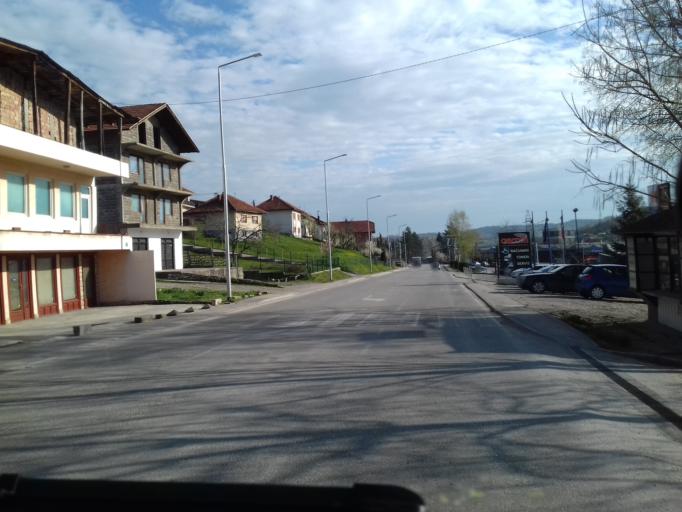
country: BA
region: Federation of Bosnia and Herzegovina
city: Tesanj
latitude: 44.6233
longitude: 17.9978
